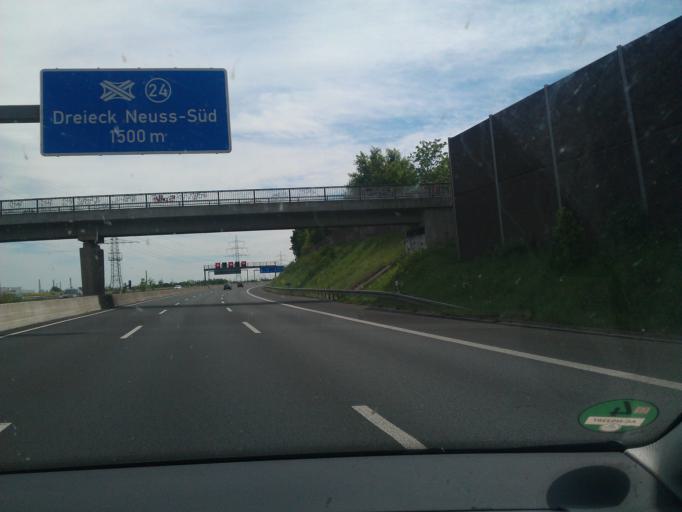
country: DE
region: North Rhine-Westphalia
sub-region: Regierungsbezirk Dusseldorf
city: Neuss
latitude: 51.1681
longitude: 6.7371
